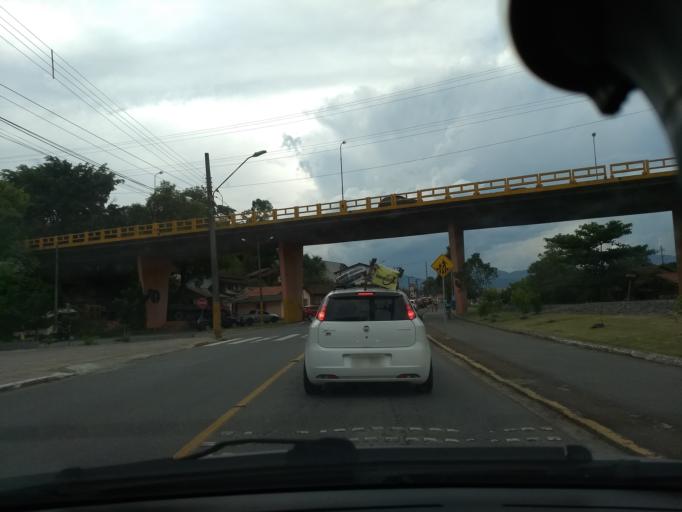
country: BR
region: Santa Catarina
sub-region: Jaragua Do Sul
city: Jaragua do Sul
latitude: -26.4779
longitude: -49.0983
